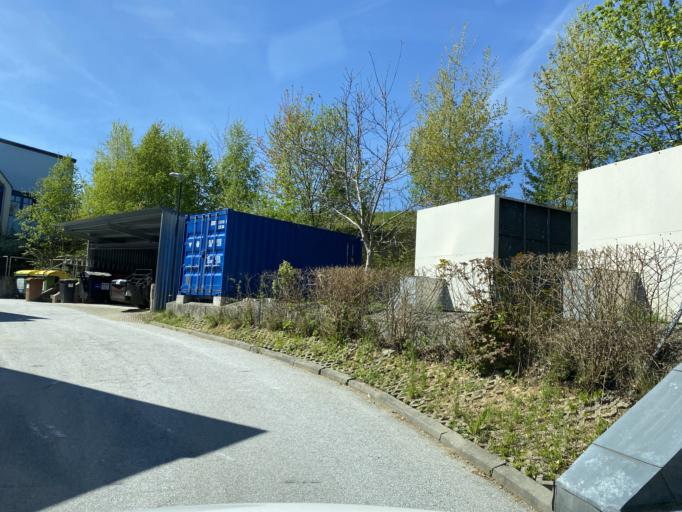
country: AT
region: Styria
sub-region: Politischer Bezirk Weiz
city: Birkfeld
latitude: 47.3533
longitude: 15.6901
